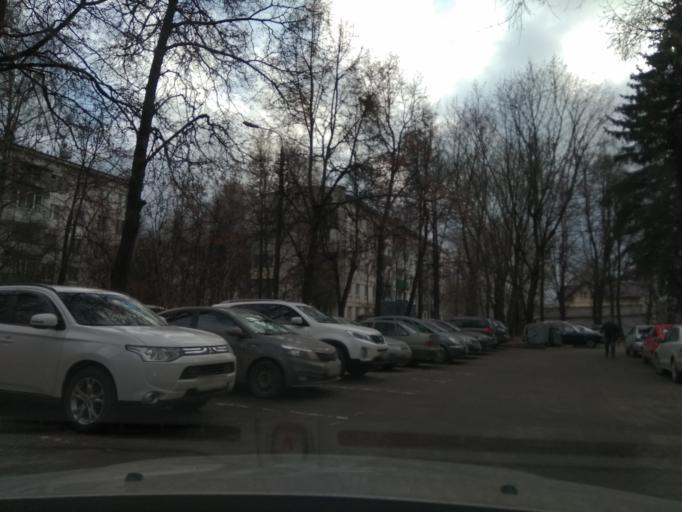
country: RU
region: Moskovskaya
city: Vidnoye
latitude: 55.5535
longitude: 37.6931
